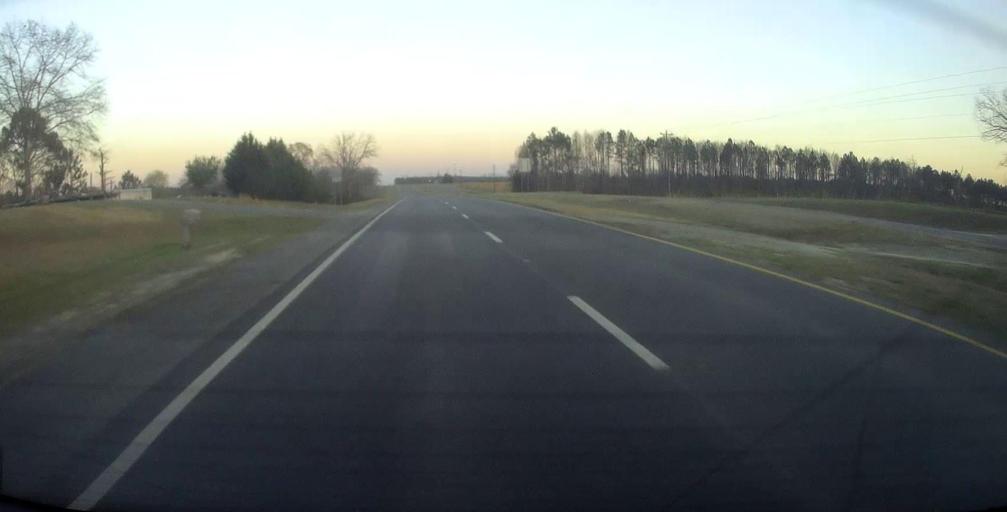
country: US
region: Georgia
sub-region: Dodge County
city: Eastman
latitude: 32.1583
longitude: -83.1474
